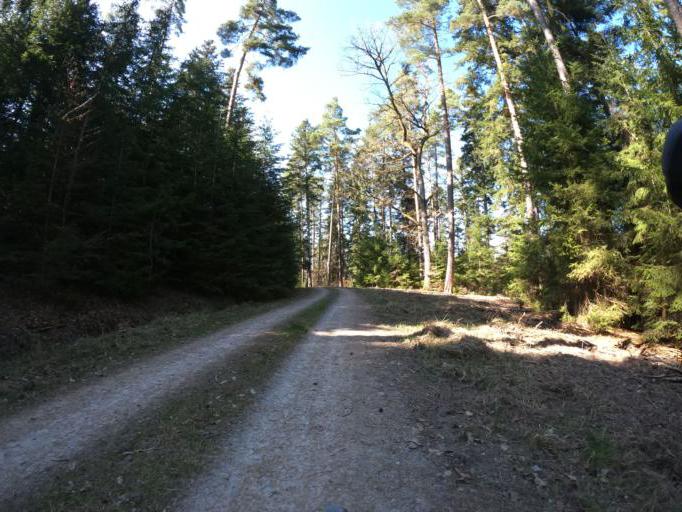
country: DE
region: Baden-Wuerttemberg
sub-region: Tuebingen Region
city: Hirrlingen
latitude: 48.4018
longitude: 8.9290
